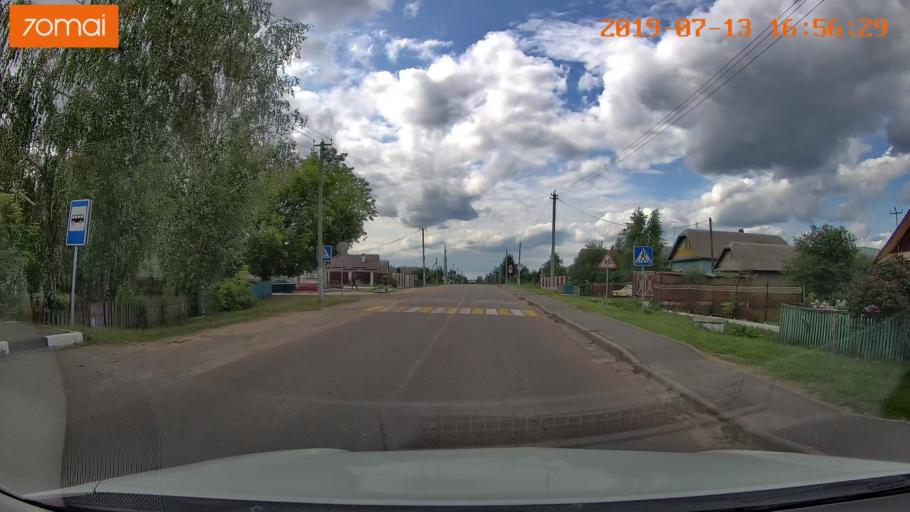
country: BY
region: Mogilev
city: Kirawsk
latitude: 53.2738
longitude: 29.4587
